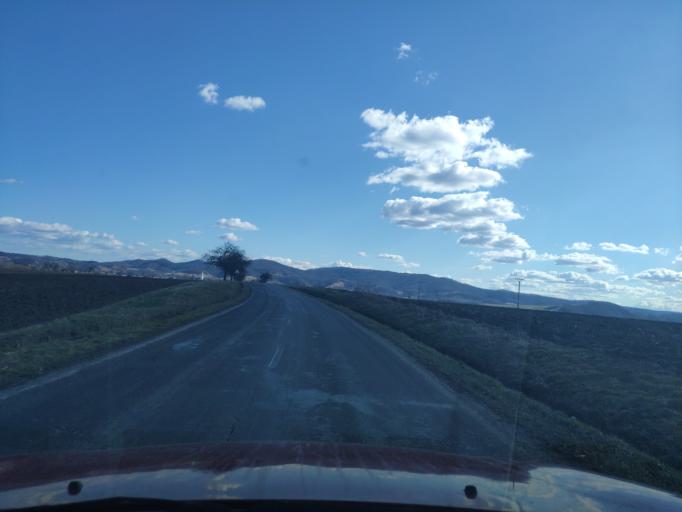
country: SK
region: Banskobystricky
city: Rimavska Sobota
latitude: 48.2828
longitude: 20.0941
